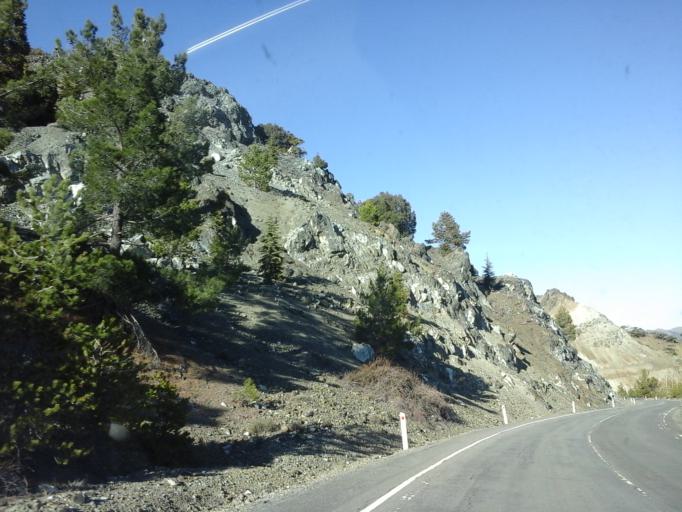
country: CY
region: Lefkosia
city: Kakopetria
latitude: 34.9323
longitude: 32.9073
